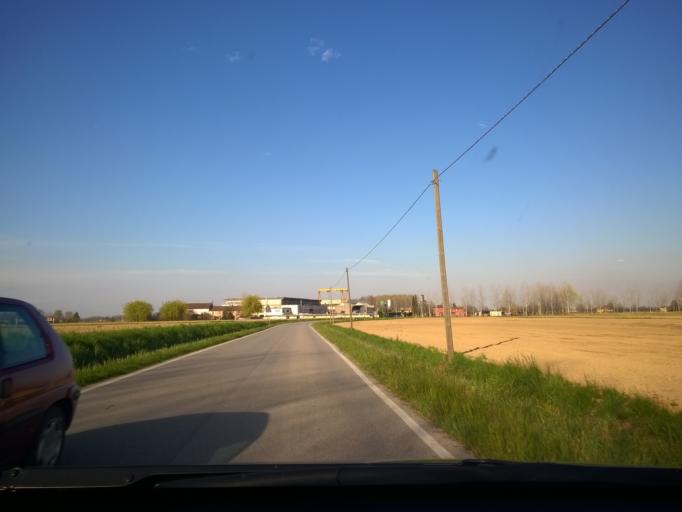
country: IT
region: Veneto
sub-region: Provincia di Treviso
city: San Biagio di Callalta
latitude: 45.7064
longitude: 12.3741
